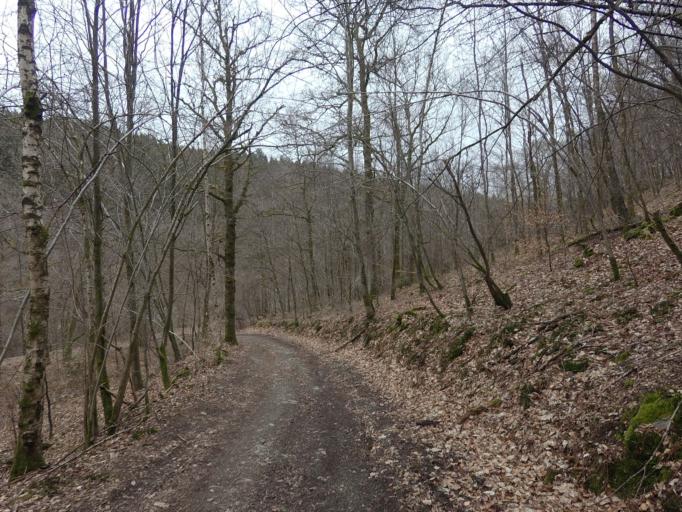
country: BE
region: Wallonia
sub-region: Province de Liege
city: Stoumont
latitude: 50.4198
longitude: 5.7464
